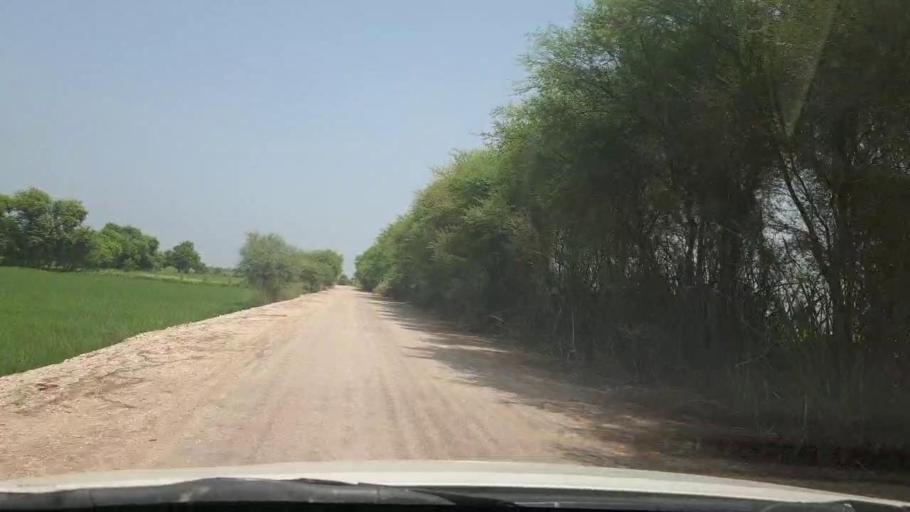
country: PK
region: Sindh
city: Rustam jo Goth
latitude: 28.0301
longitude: 68.7955
